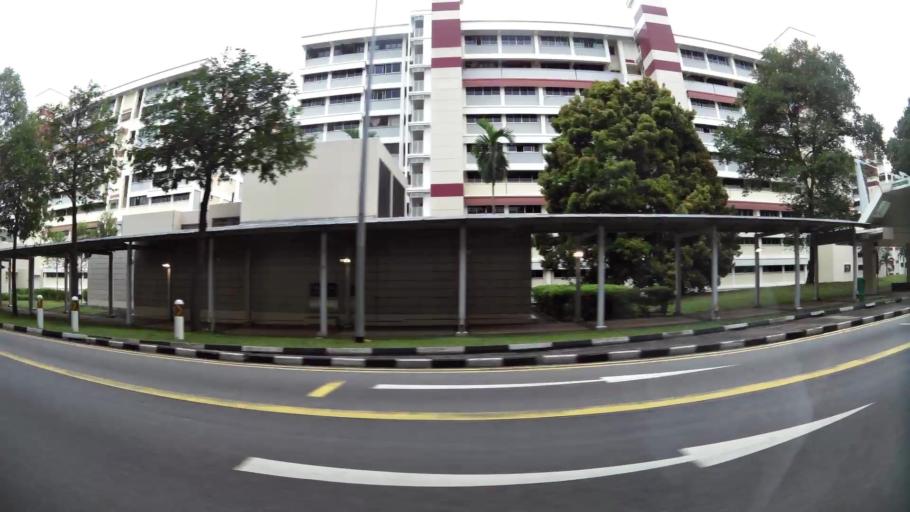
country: SG
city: Singapore
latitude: 1.3487
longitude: 103.8731
